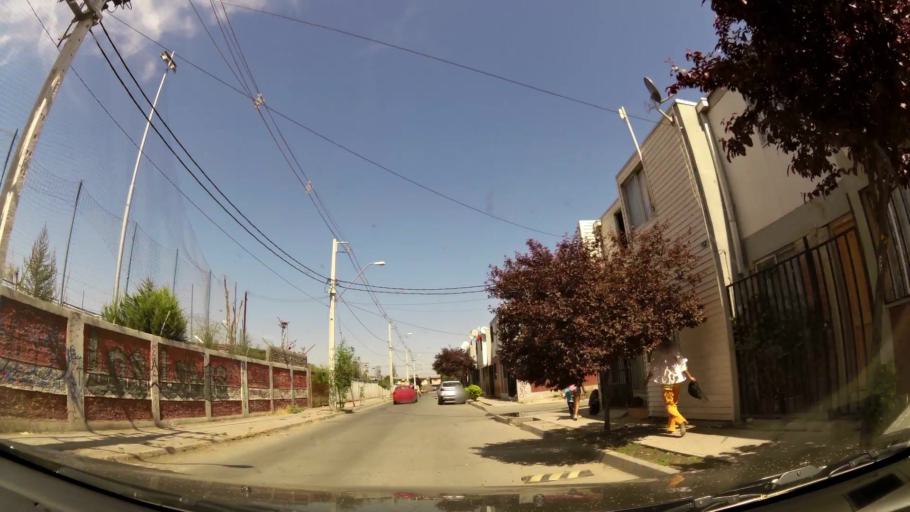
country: CL
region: Santiago Metropolitan
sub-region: Provincia de Santiago
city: Lo Prado
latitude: -33.3968
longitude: -70.7499
